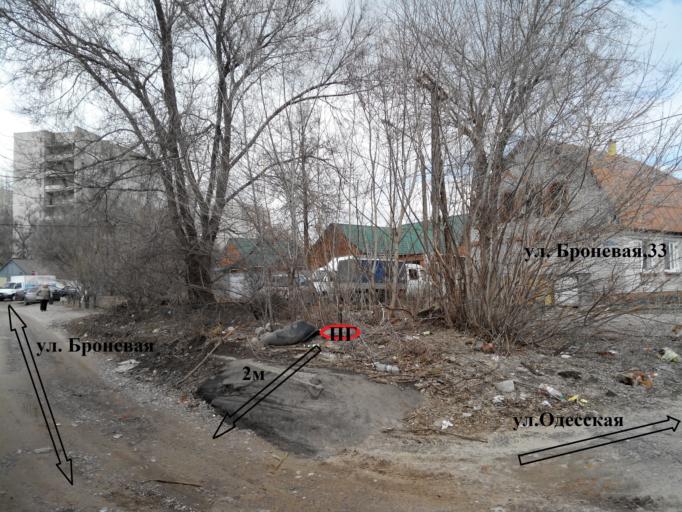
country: RU
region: Voronezj
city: Voronezh
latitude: 51.6367
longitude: 39.1569
